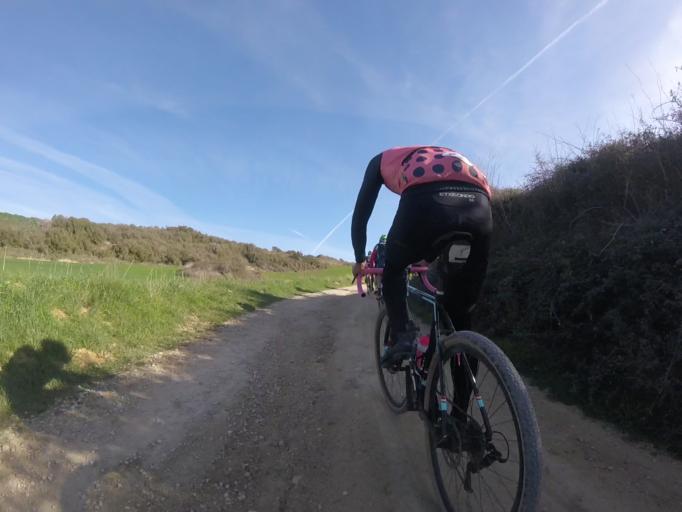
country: ES
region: Navarre
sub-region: Provincia de Navarra
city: Yerri
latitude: 42.7028
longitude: -1.9657
